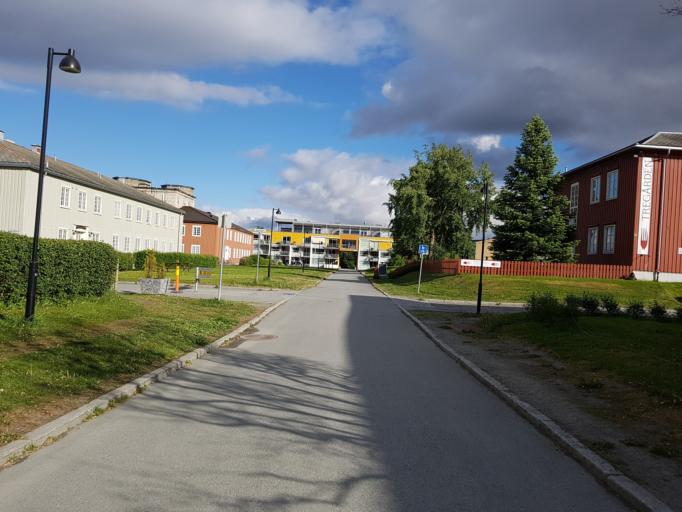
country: NO
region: Sor-Trondelag
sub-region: Trondheim
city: Trondheim
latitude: 63.4317
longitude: 10.4431
